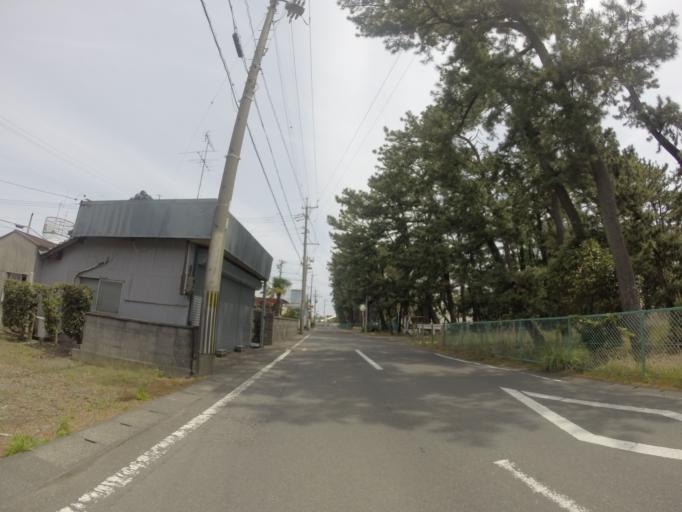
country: JP
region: Shizuoka
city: Yaizu
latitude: 34.8156
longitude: 138.3249
